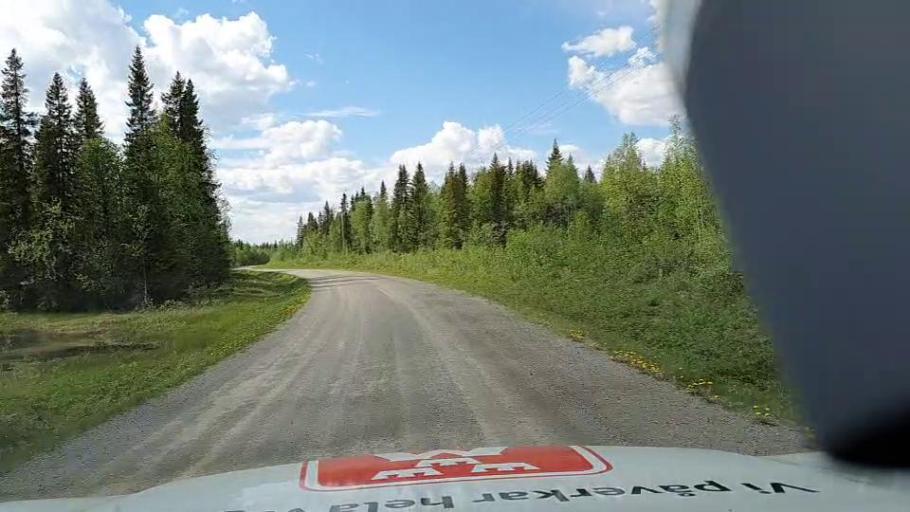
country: SE
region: Vaesterbotten
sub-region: Vilhelmina Kommun
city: Sjoberg
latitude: 64.5413
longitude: 15.7247
